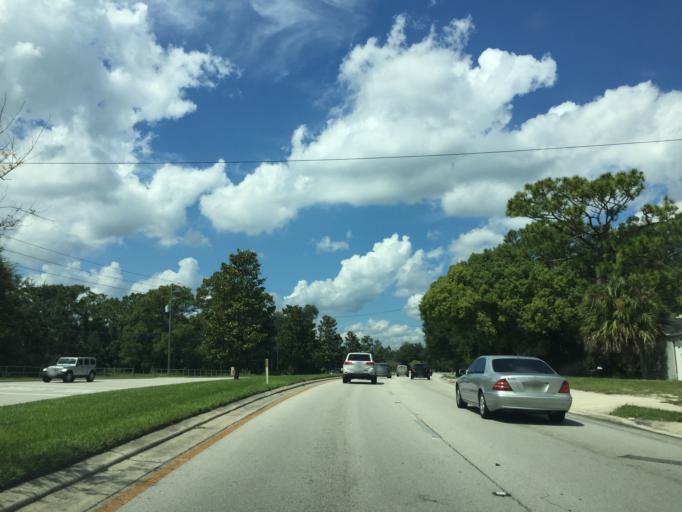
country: US
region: Florida
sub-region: Seminole County
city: Casselberry
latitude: 28.6754
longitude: -81.3183
